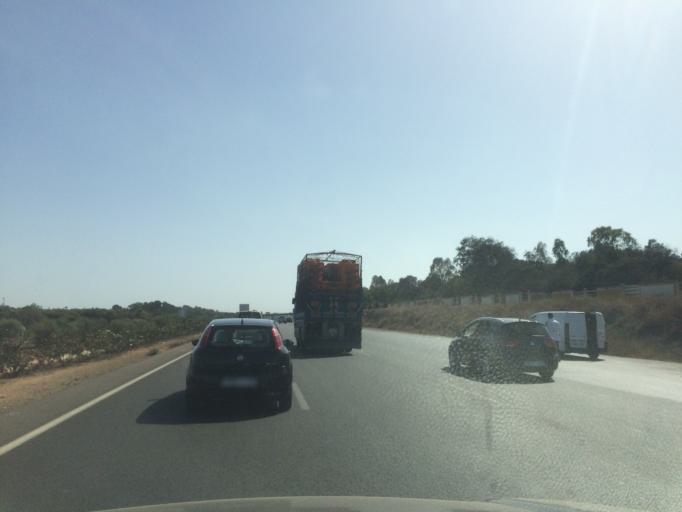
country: MA
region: Rabat-Sale-Zemmour-Zaer
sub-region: Skhirate-Temara
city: Temara
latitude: 33.9463
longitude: -6.9216
